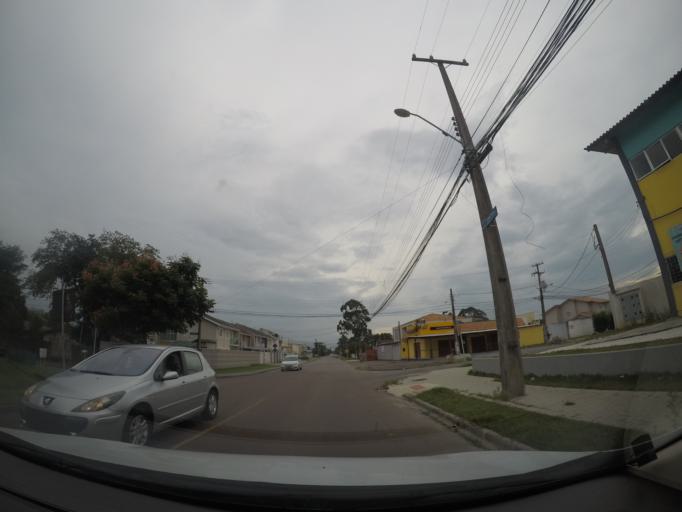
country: BR
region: Parana
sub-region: Curitiba
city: Curitiba
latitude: -25.4700
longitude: -49.2445
